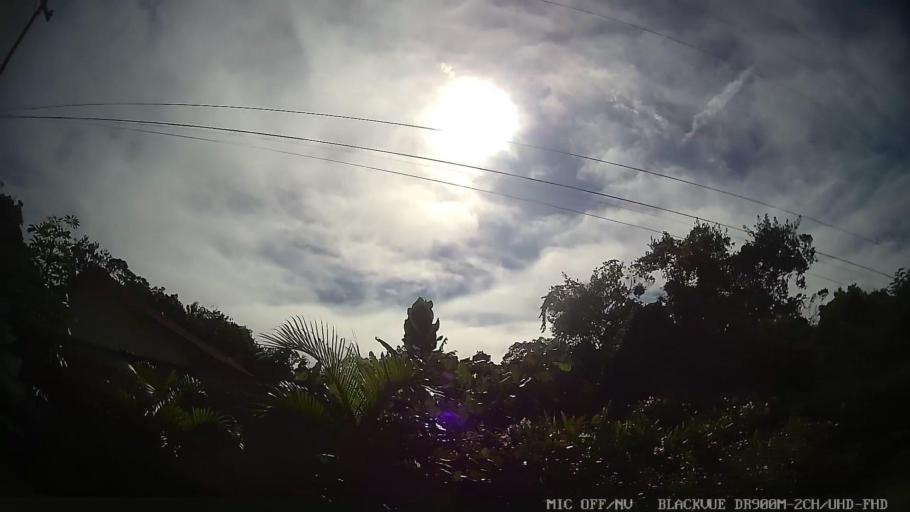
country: BR
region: Sao Paulo
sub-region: Peruibe
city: Peruibe
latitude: -24.2256
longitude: -46.9178
